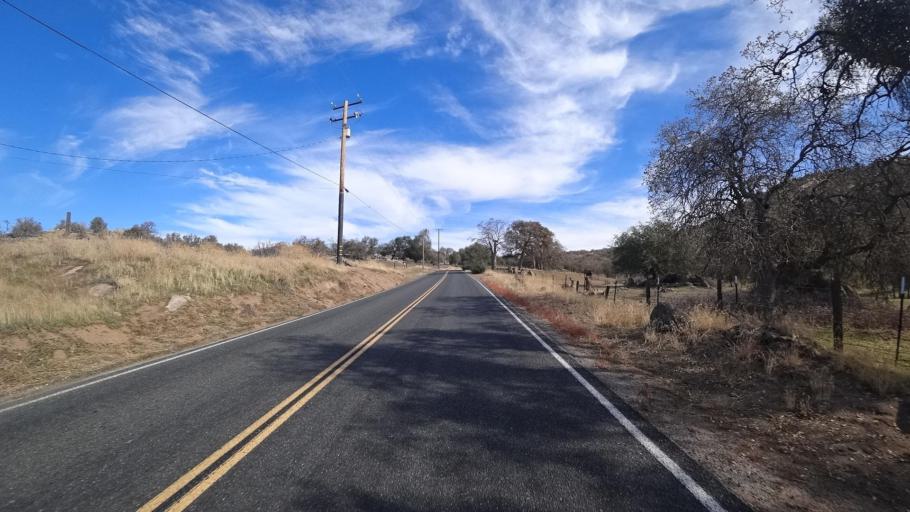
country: US
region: California
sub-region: Kern County
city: Alta Sierra
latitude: 35.6433
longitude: -118.7986
